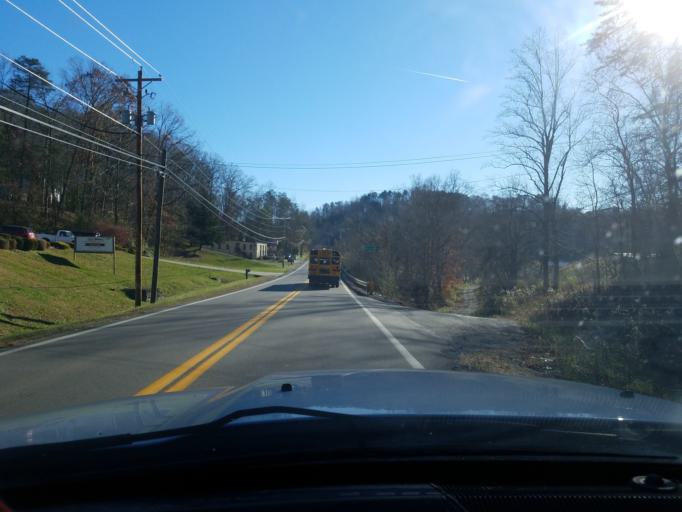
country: US
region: West Virginia
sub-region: Putnam County
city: Teays Valley
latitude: 38.4703
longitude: -81.9347
